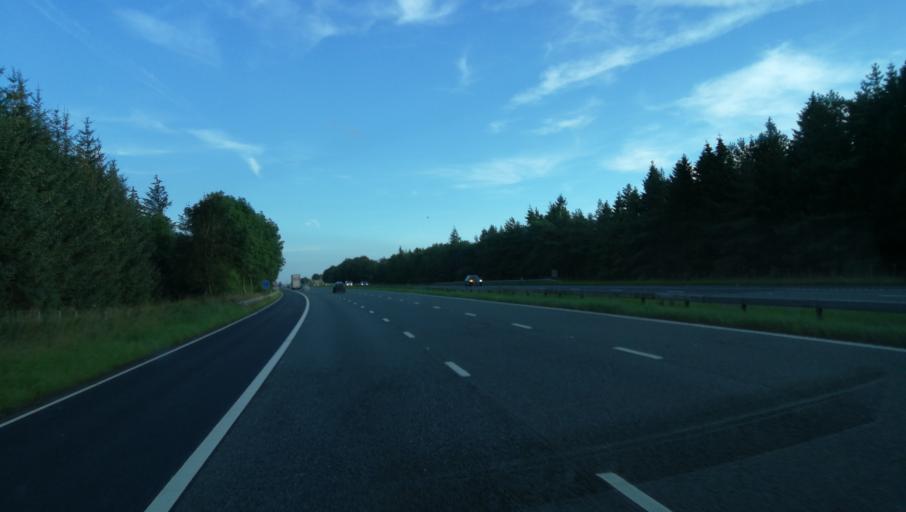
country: GB
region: England
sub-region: Cumbria
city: Penrith
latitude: 54.5841
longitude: -2.6998
